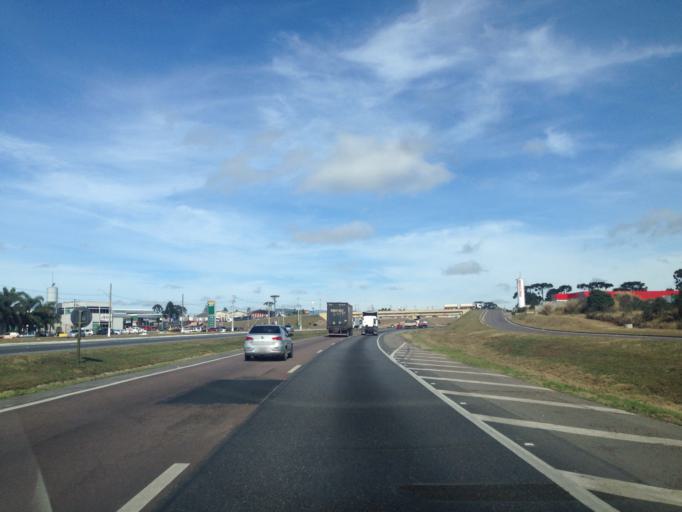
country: BR
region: Parana
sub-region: Sao Jose Dos Pinhais
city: Sao Jose dos Pinhais
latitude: -25.5574
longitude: -49.1501
